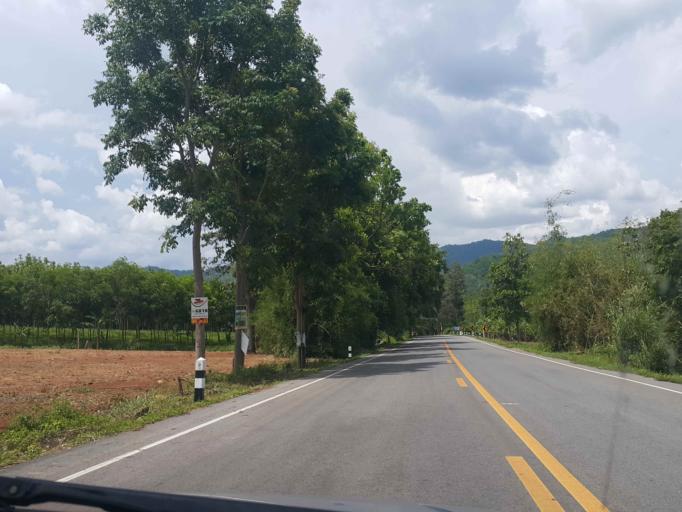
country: TH
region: Nan
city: Ban Luang
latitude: 18.8642
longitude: 100.4648
